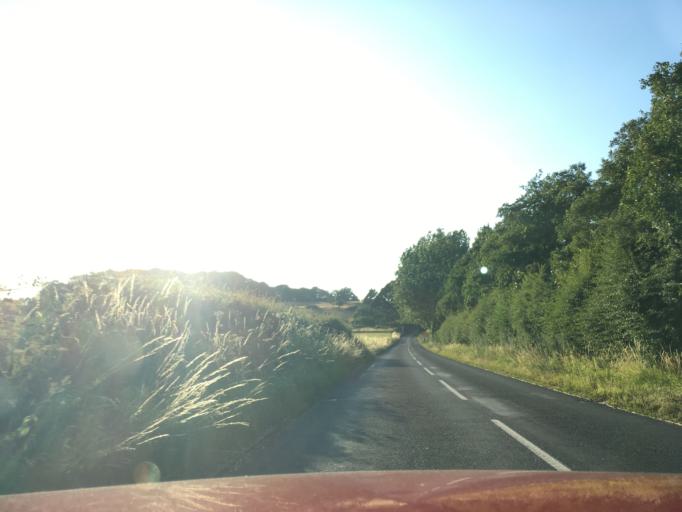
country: GB
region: England
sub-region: Hampshire
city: Tadley
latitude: 51.4120
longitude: -1.1389
